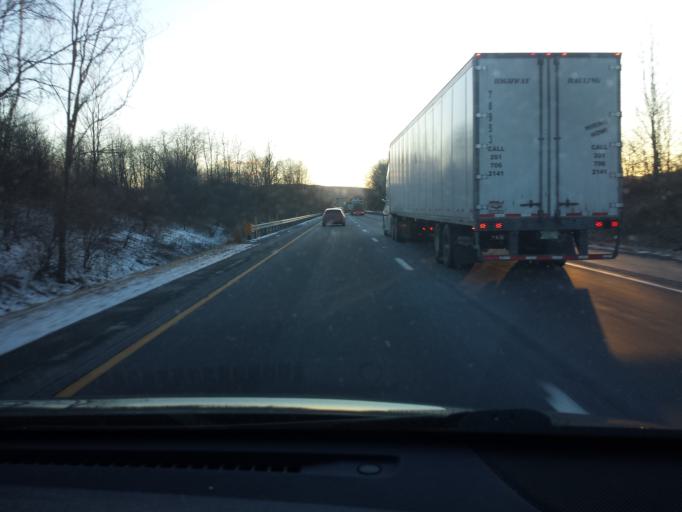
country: US
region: Pennsylvania
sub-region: Centre County
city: Zion
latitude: 40.9830
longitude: -77.6228
